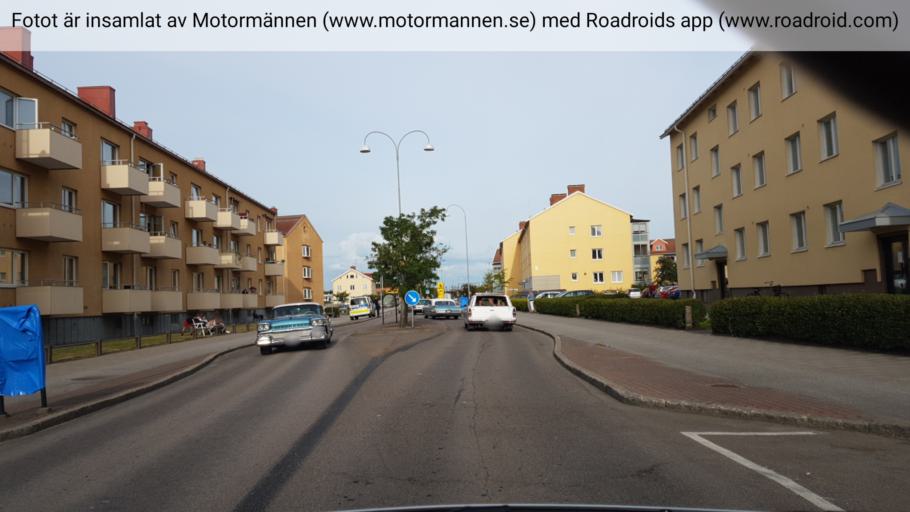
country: SE
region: Vaestra Goetaland
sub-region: Lidkopings Kommun
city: Lidkoping
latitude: 58.4991
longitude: 13.1678
